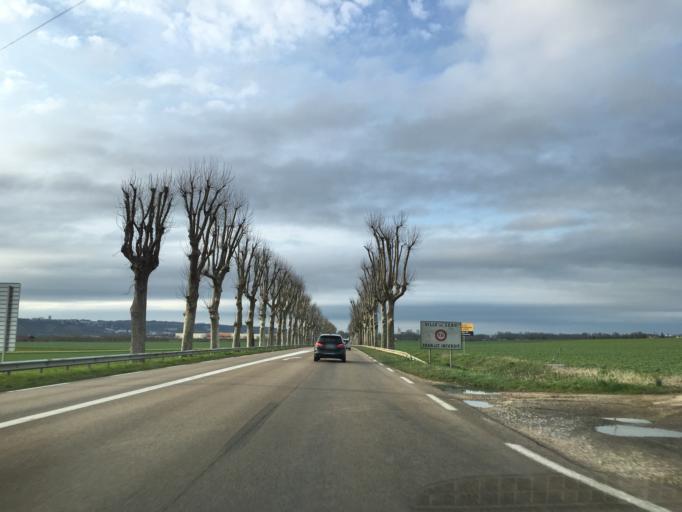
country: FR
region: Bourgogne
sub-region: Departement de l'Yonne
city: Maillot
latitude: 48.1639
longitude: 3.3007
